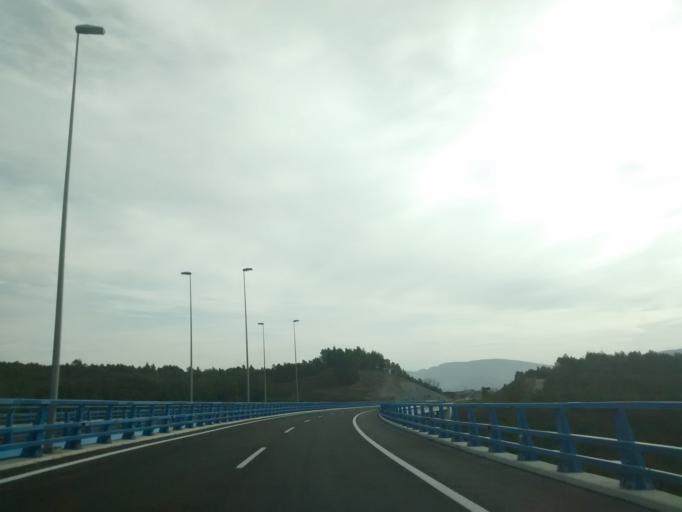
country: ES
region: Navarre
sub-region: Provincia de Navarra
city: Yesa
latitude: 42.6254
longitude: -1.1725
